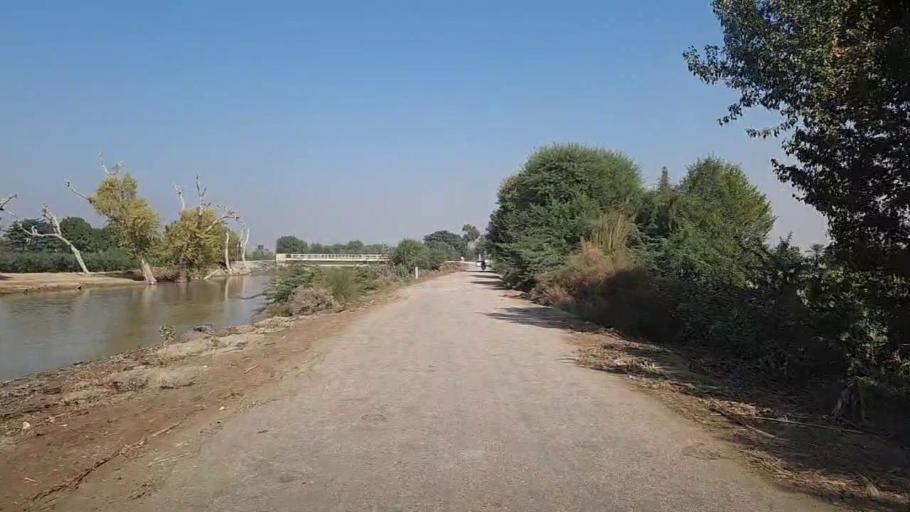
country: PK
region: Sindh
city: Bozdar
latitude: 27.2040
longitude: 68.6668
